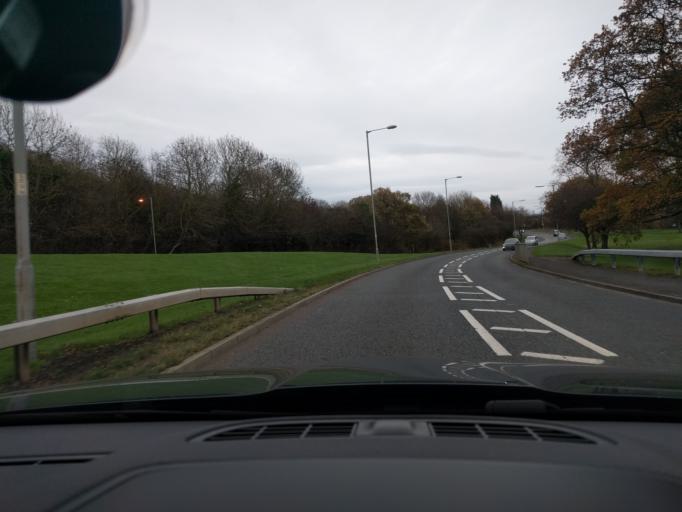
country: GB
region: England
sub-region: Northumberland
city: Ashington
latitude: 55.1673
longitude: -1.5742
